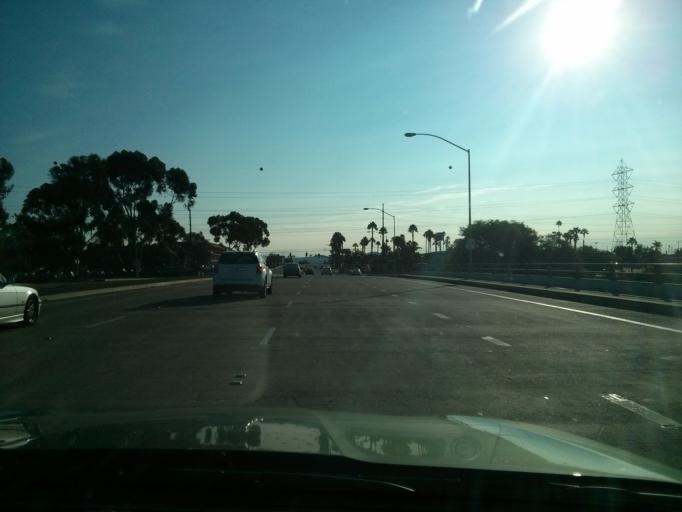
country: US
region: California
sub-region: San Diego County
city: San Diego
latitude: 32.8216
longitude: -117.1626
